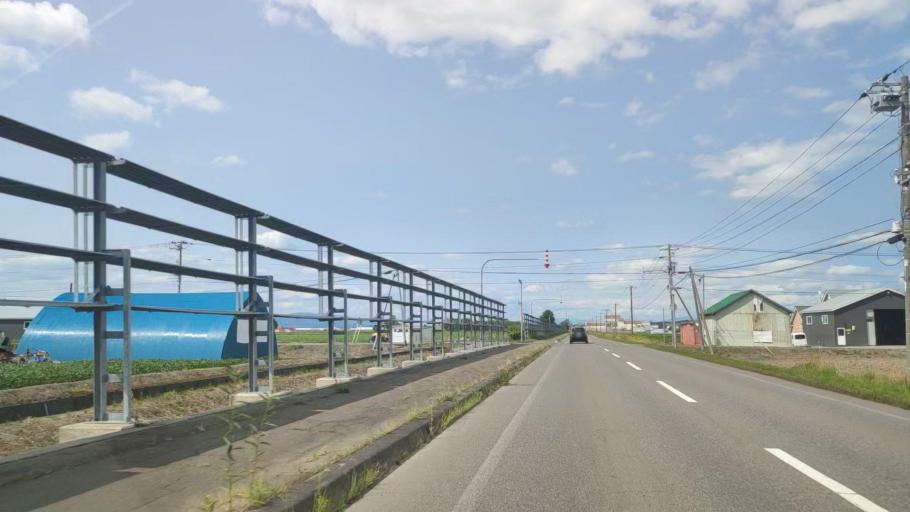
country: JP
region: Hokkaido
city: Nayoro
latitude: 44.1953
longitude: 142.4159
